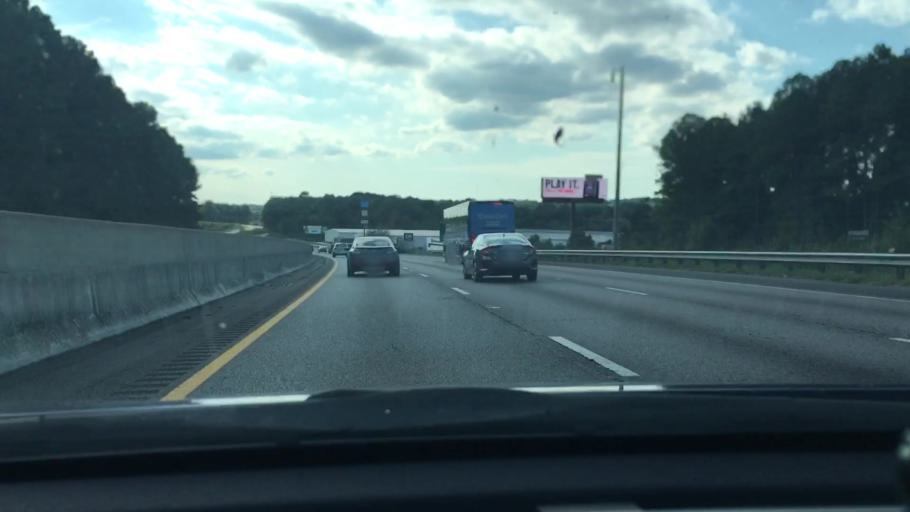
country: US
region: South Carolina
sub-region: Richland County
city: Columbia
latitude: 34.0662
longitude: -81.0389
